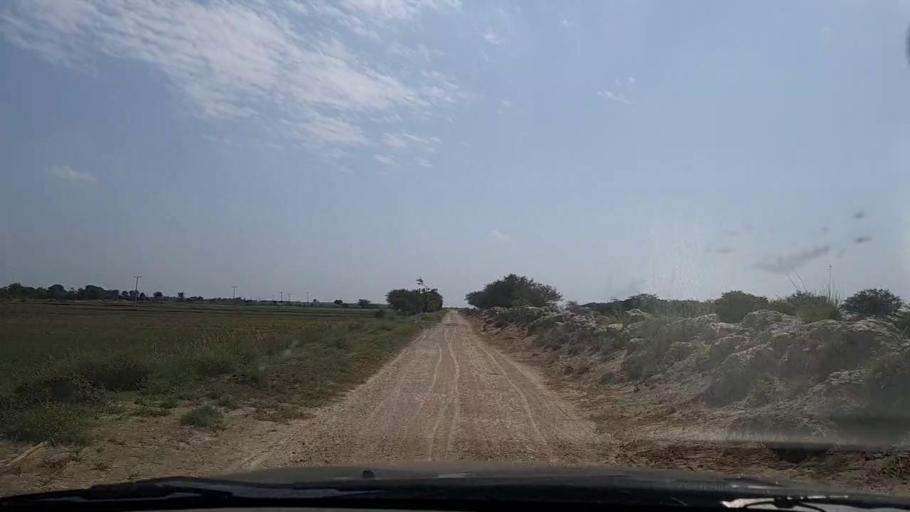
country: PK
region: Sindh
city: Mirpur Batoro
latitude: 24.5845
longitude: 68.1964
